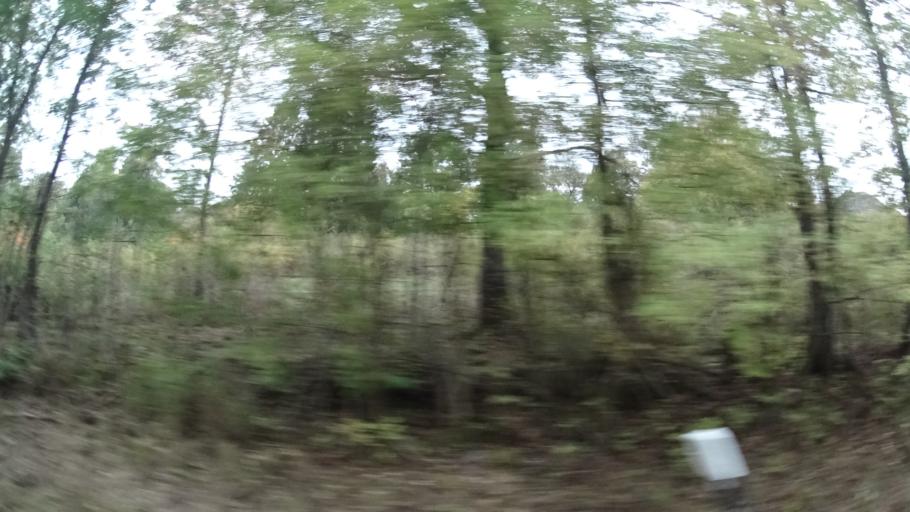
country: DE
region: Hesse
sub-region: Regierungsbezirk Kassel
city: Hilders
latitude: 50.5637
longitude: 10.0212
